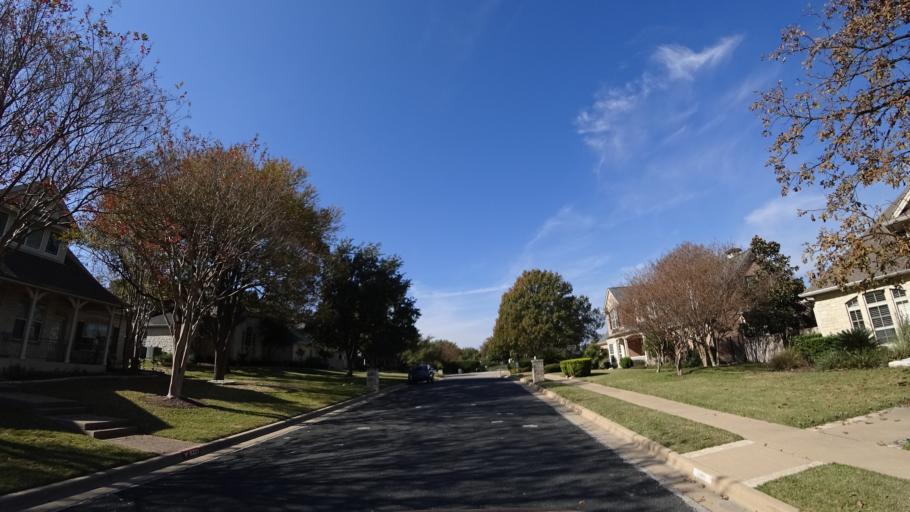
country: US
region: Texas
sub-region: Williamson County
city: Jollyville
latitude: 30.3749
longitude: -97.7732
